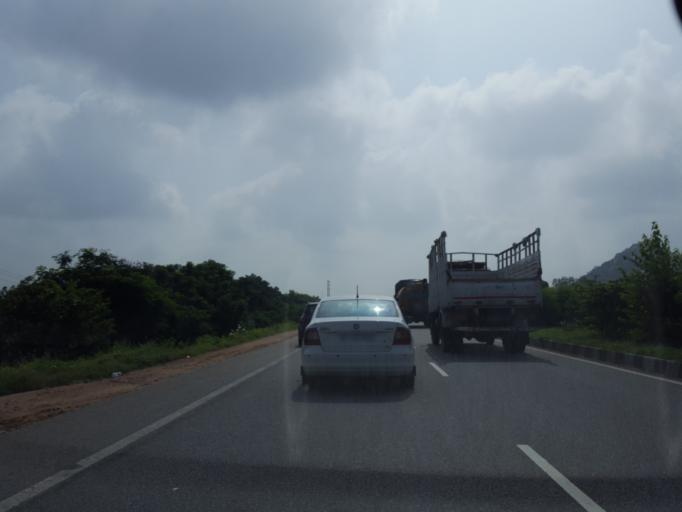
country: IN
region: Telangana
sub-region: Nalgonda
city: Gudur
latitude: 17.2751
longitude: 78.8137
